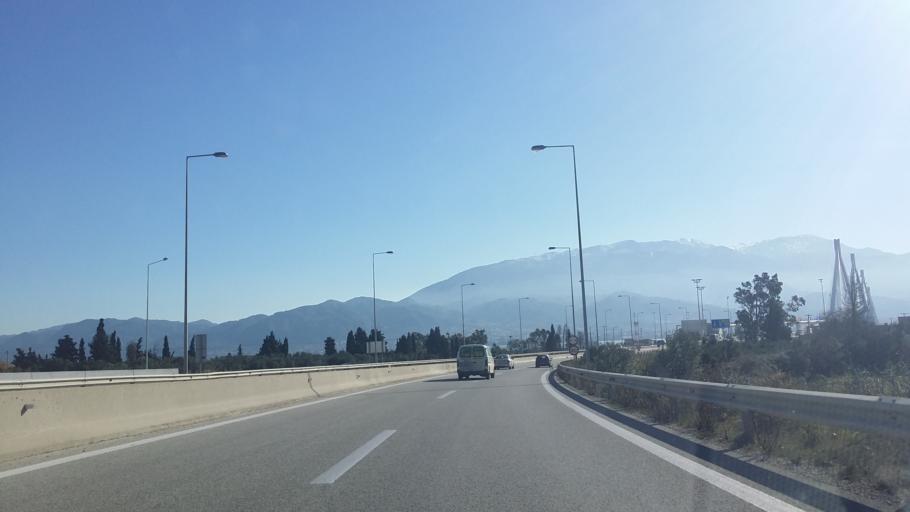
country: GR
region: West Greece
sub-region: Nomos Aitolias kai Akarnanias
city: Antirrio
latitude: 38.3383
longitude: 21.7625
